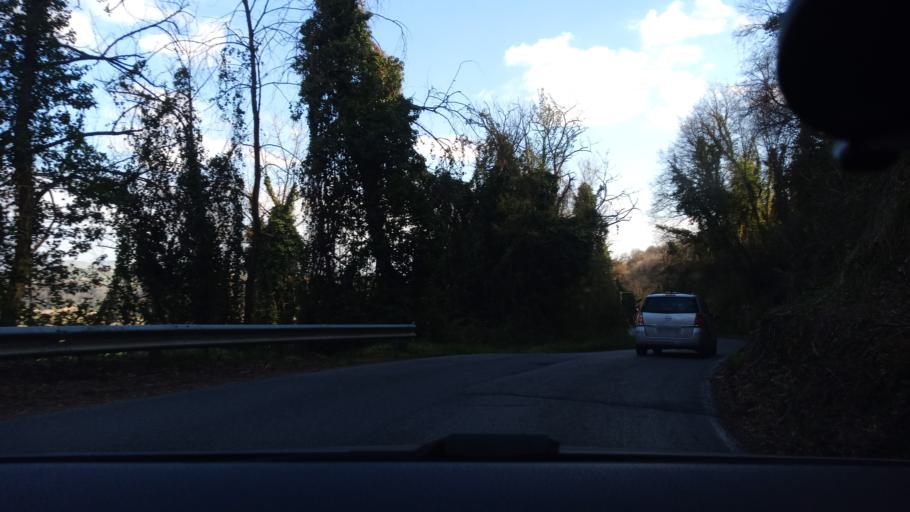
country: IT
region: Latium
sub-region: Citta metropolitana di Roma Capitale
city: Torrita Tiberina
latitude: 42.2417
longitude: 12.6215
